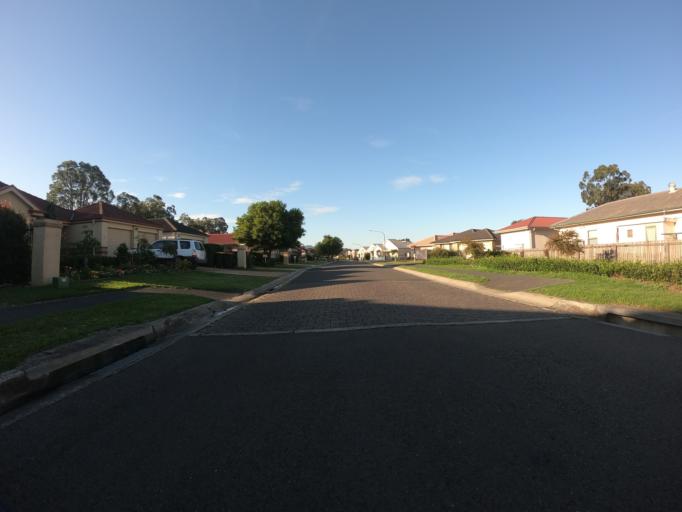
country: AU
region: New South Wales
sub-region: Wollongong
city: Dapto
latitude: -34.4897
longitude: 150.7948
